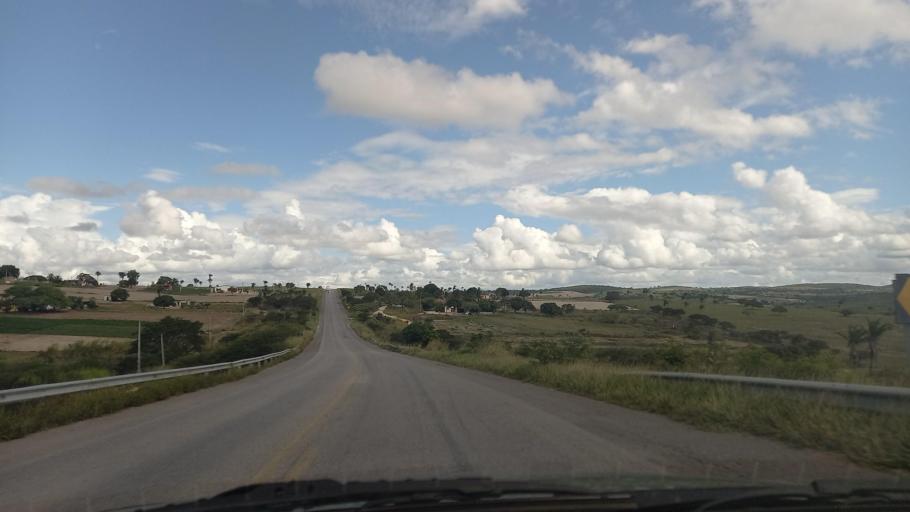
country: BR
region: Pernambuco
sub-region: Lajedo
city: Lajedo
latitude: -8.7283
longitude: -36.4318
